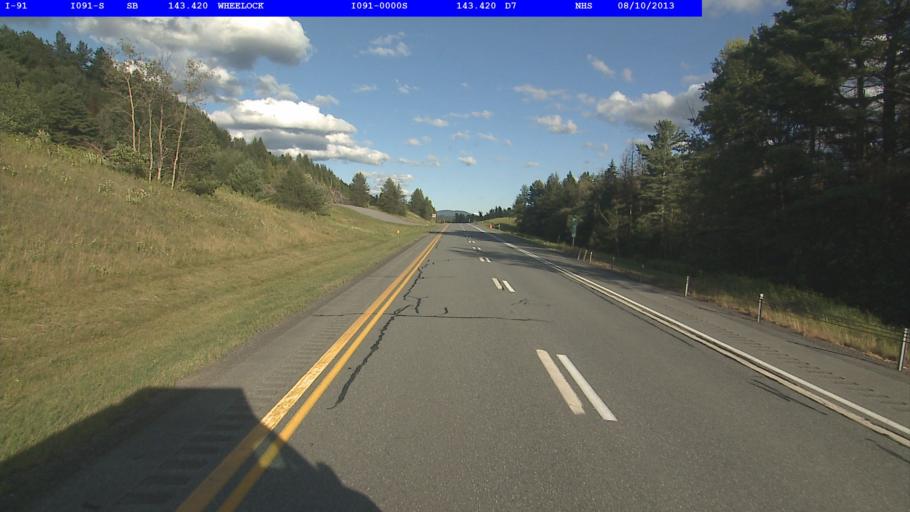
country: US
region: Vermont
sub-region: Caledonia County
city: Lyndonville
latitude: 44.5865
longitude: -72.0752
